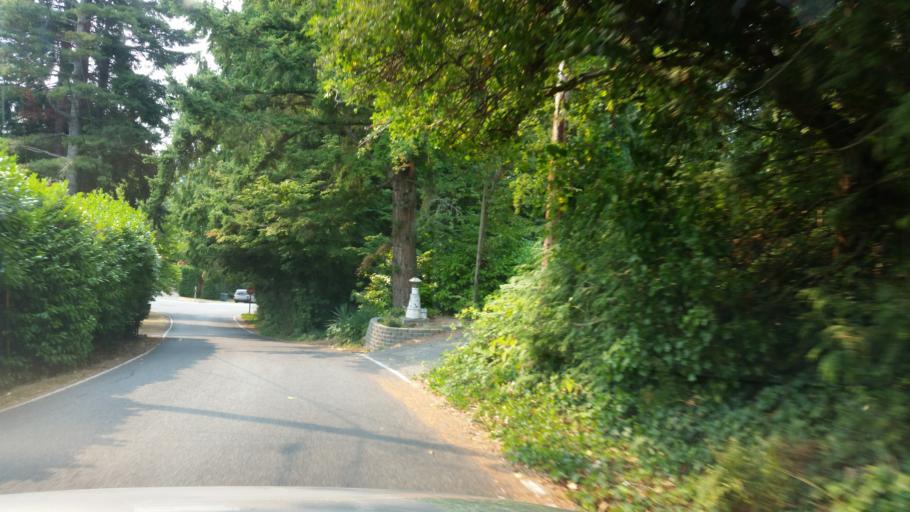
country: US
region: Washington
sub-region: Snohomish County
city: Edmonds
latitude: 47.8186
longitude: -122.3510
